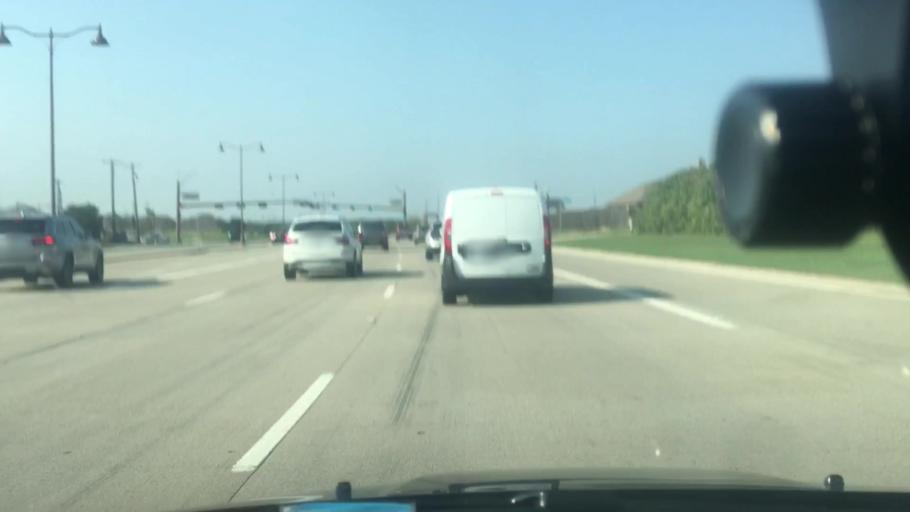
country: US
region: Texas
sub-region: Collin County
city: Prosper
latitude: 33.2465
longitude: -96.7851
